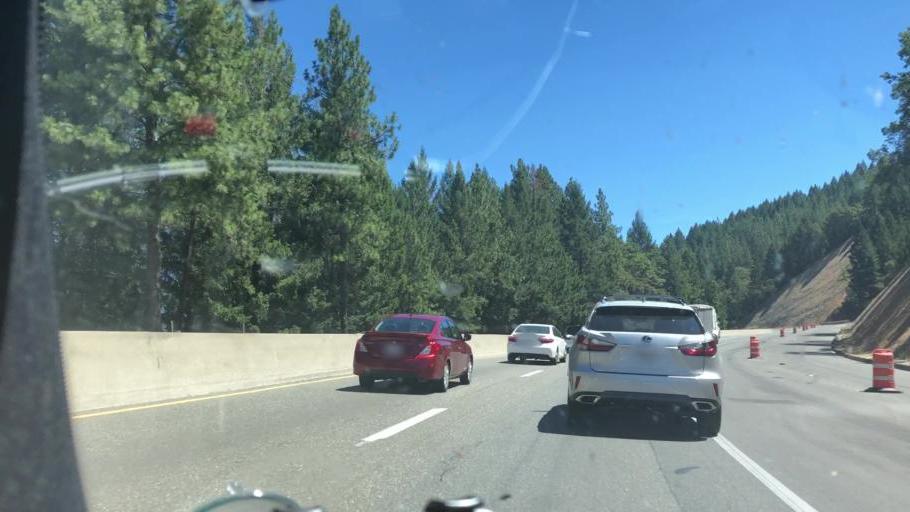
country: US
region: California
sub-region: Placer County
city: Colfax
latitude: 39.1323
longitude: -120.9343
